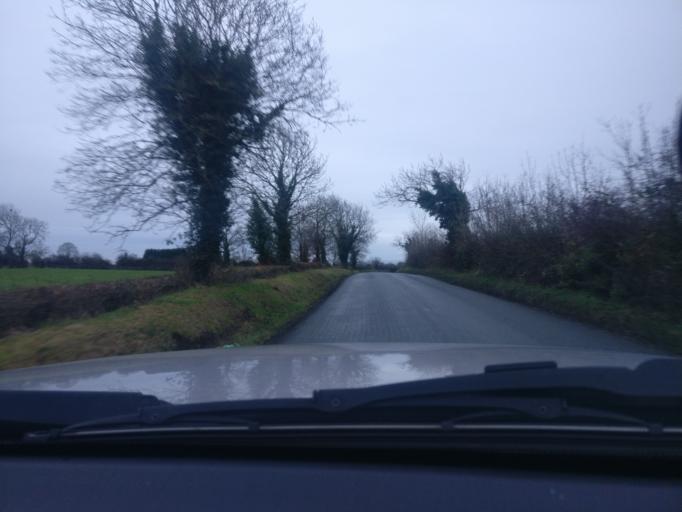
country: IE
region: Leinster
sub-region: Kildare
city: Maynooth
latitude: 53.4197
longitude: -6.6142
